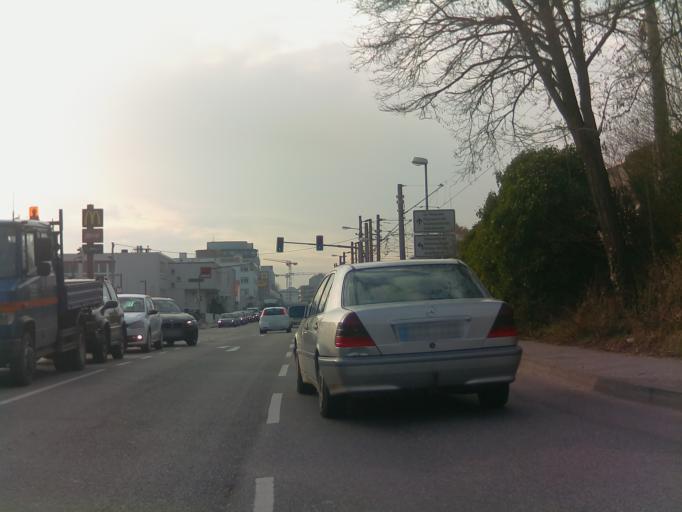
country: DE
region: Baden-Wuerttemberg
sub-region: Regierungsbezirk Stuttgart
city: Leinfelden-Echterdingen
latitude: 48.7223
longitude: 9.1313
